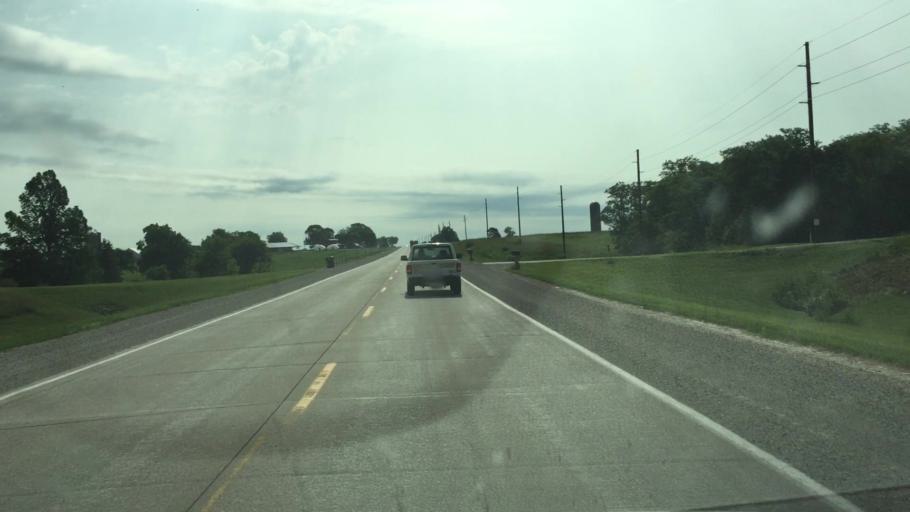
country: US
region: Illinois
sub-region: Hancock County
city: Nauvoo
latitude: 40.6390
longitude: -91.5389
